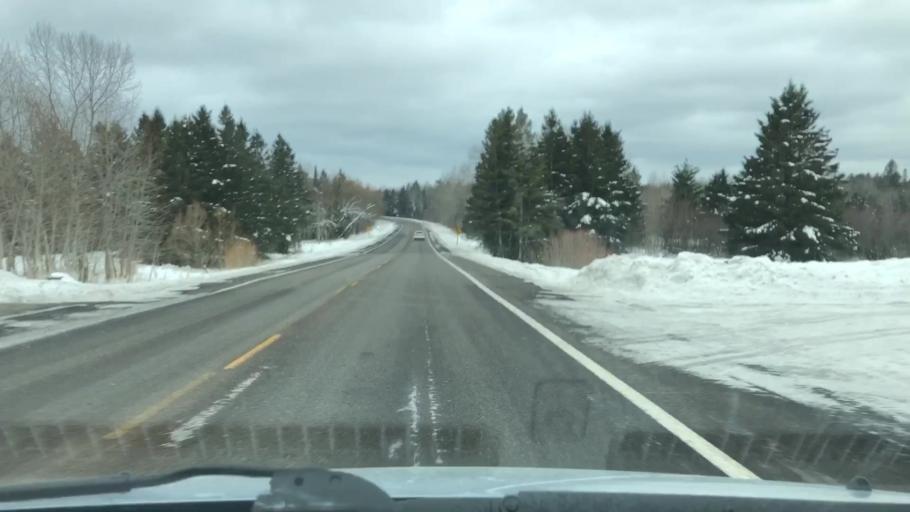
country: US
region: Minnesota
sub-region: Carlton County
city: Esko
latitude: 46.6759
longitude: -92.3790
